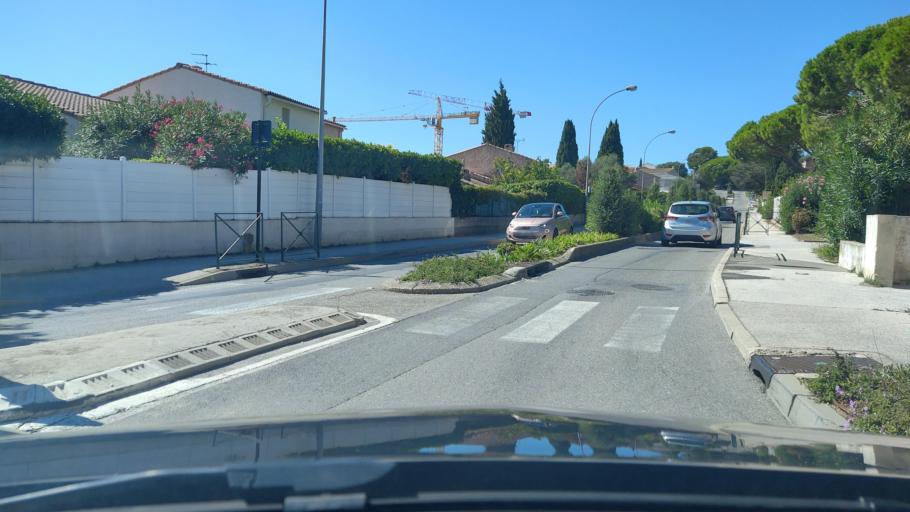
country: FR
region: Provence-Alpes-Cote d'Azur
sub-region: Departement du Var
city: Sanary-sur-Mer
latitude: 43.1289
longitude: 5.7985
